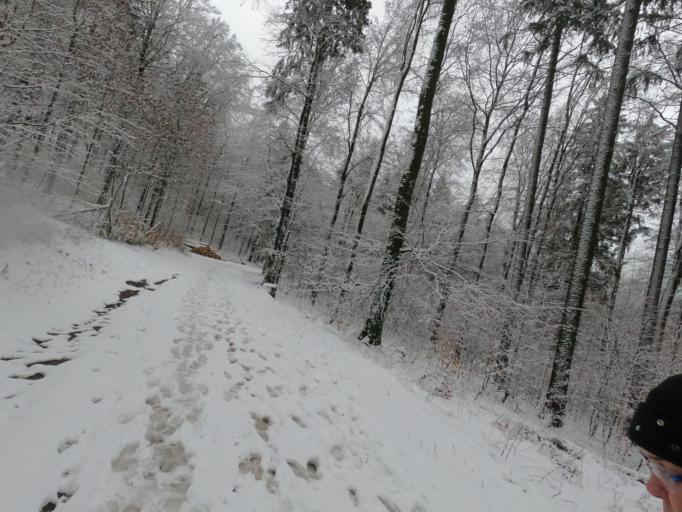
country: DE
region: Hesse
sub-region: Regierungsbezirk Darmstadt
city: Glashutten
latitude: 50.2271
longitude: 8.4255
